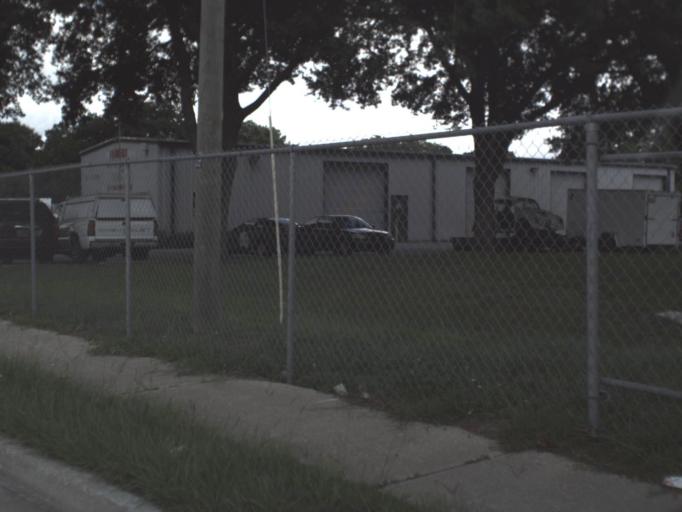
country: US
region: Florida
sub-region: Hillsborough County
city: East Lake-Orient Park
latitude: 27.9815
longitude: -82.4152
